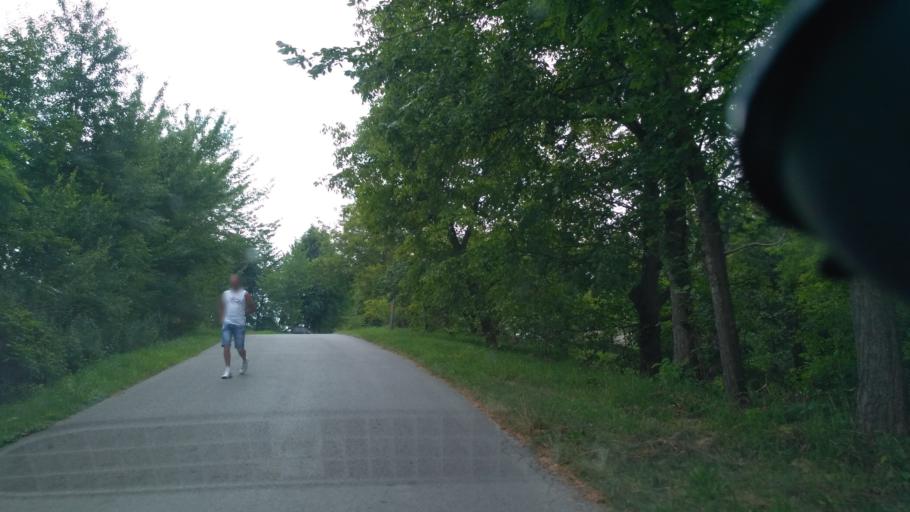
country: PL
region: Subcarpathian Voivodeship
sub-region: Powiat przeworski
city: Lopuszka Wielka
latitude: 49.9174
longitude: 22.4118
